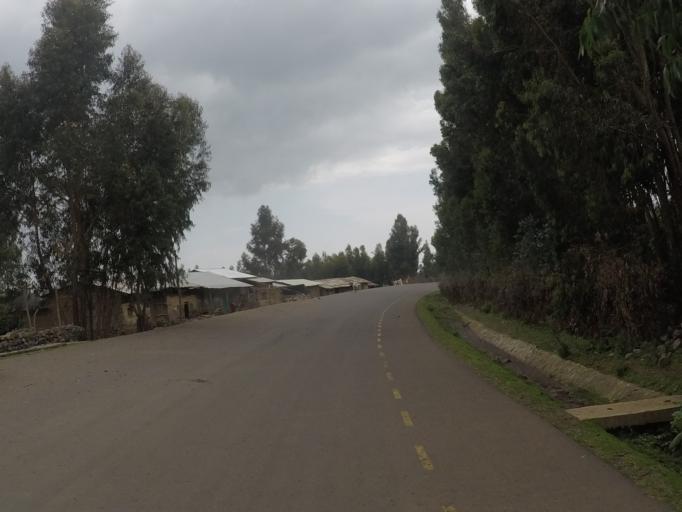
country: ET
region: Amhara
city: Dabat
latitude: 13.0633
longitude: 37.8232
